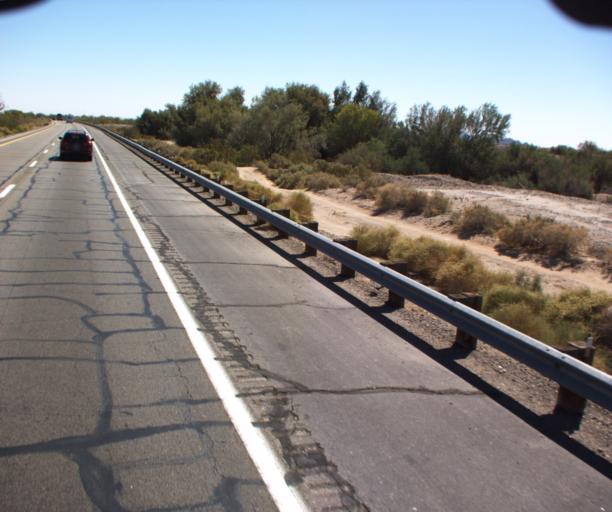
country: US
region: Arizona
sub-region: Yuma County
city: Wellton
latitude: 32.6500
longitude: -114.2150
